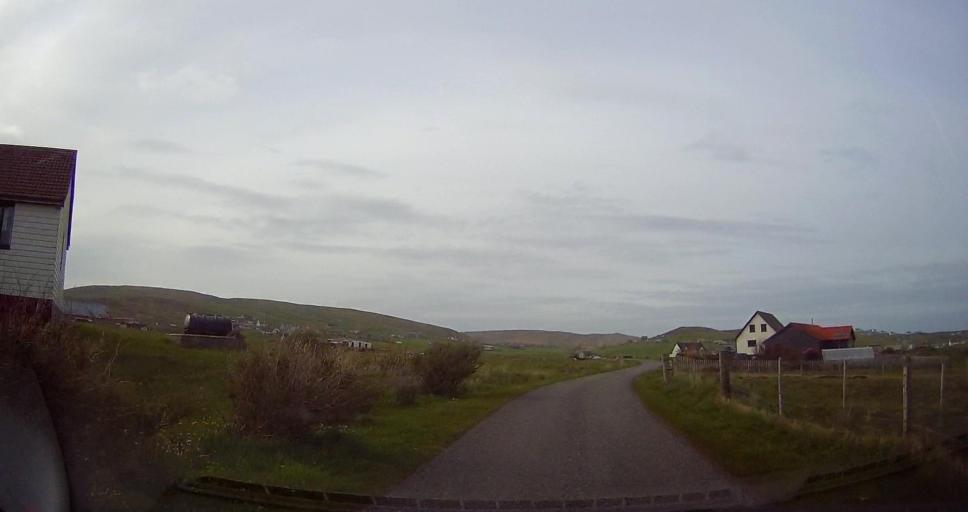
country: GB
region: Scotland
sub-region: Shetland Islands
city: Sandwick
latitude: 60.0393
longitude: -1.2179
